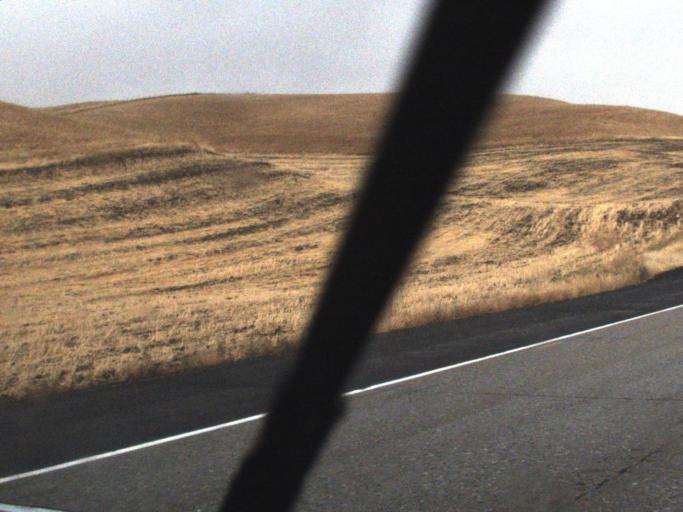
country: US
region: Washington
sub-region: Whitman County
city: Colfax
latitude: 47.0729
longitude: -117.3828
